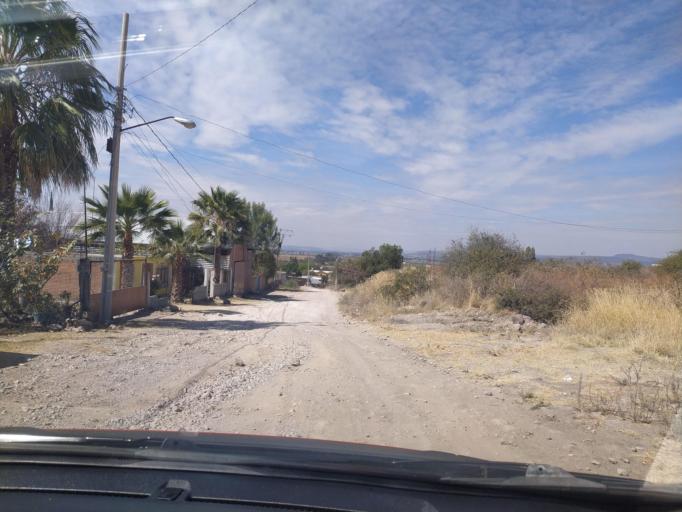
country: MX
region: Guanajuato
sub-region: San Francisco del Rincon
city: San Ignacio de Hidalgo
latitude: 20.8816
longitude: -101.8488
